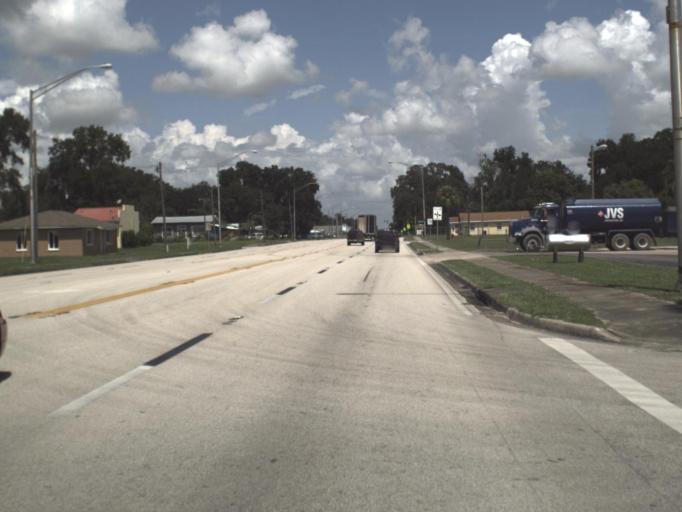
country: US
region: Florida
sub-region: Polk County
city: Fort Meade
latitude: 27.7408
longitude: -81.8014
